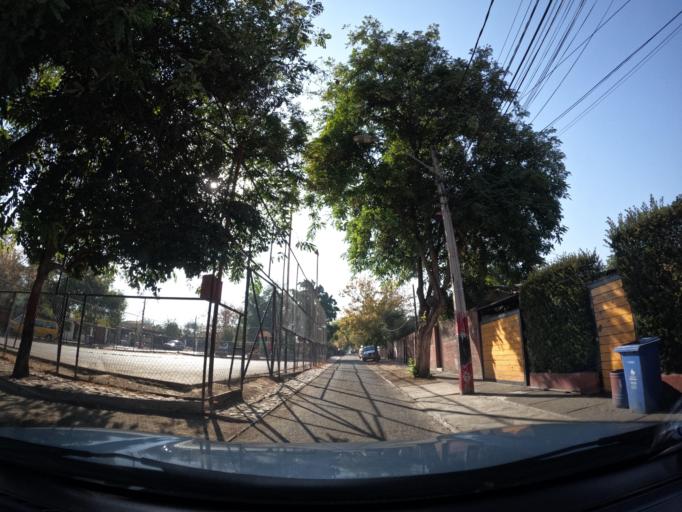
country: CL
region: Santiago Metropolitan
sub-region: Provincia de Santiago
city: Villa Presidente Frei, Nunoa, Santiago, Chile
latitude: -33.5065
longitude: -70.5710
